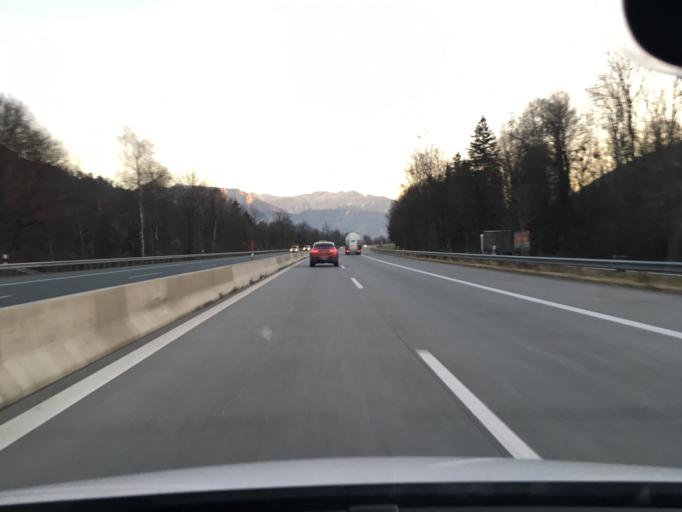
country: AT
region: Tyrol
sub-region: Politischer Bezirk Kufstein
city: Erl
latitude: 47.7019
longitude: 12.1594
